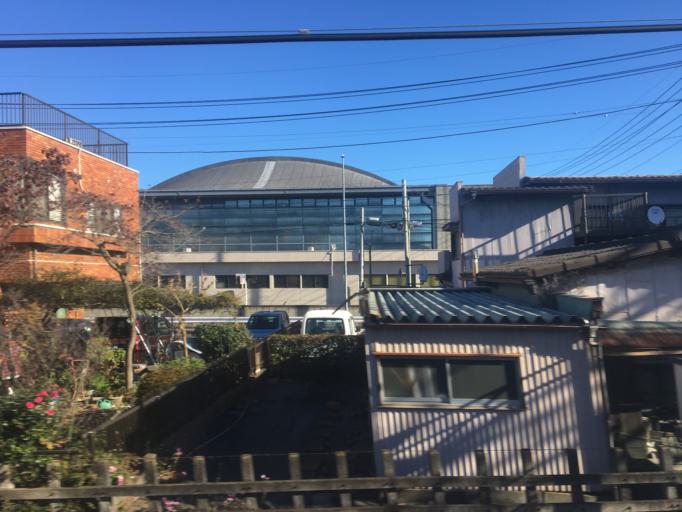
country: JP
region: Saitama
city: Sakado
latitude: 35.9553
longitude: 139.4009
